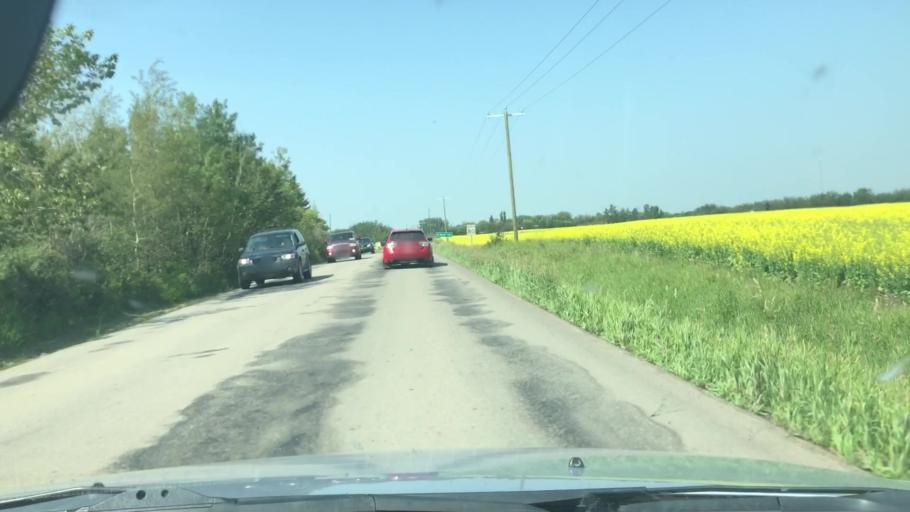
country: CA
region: Alberta
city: St. Albert
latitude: 53.5122
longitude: -113.7154
